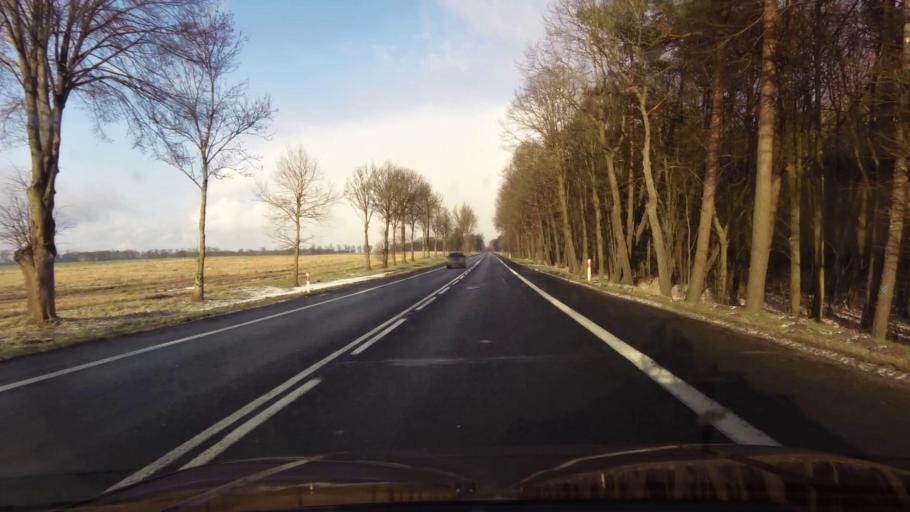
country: PL
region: West Pomeranian Voivodeship
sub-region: Powiat bialogardzki
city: Bialogard
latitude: 54.0918
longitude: 15.9911
